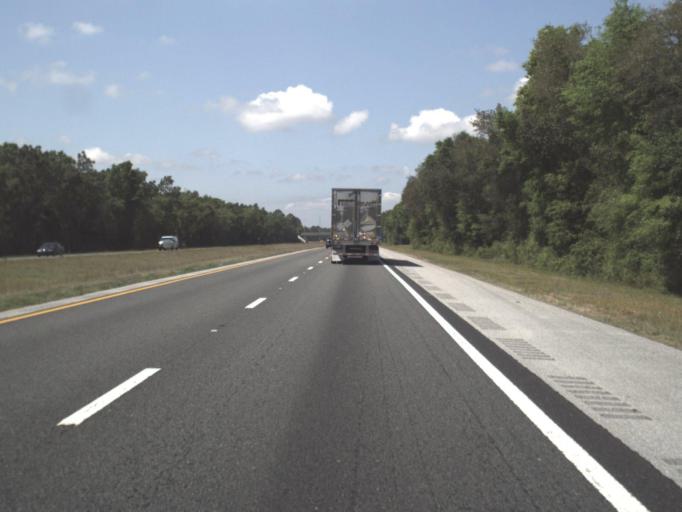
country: US
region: Florida
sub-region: Santa Rosa County
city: East Milton
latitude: 30.5986
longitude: -86.9945
